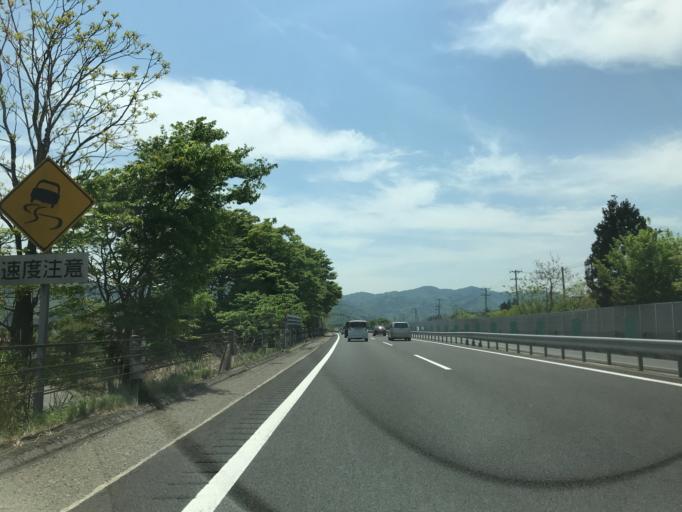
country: JP
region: Miyagi
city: Shiroishi
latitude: 37.9814
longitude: 140.6088
